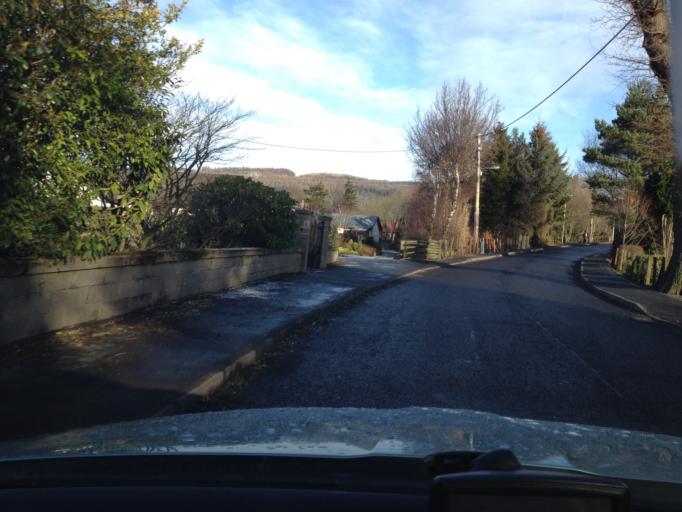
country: GB
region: Scotland
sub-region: Perth and Kinross
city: Bridge of Earn
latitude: 56.3456
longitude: -3.4075
